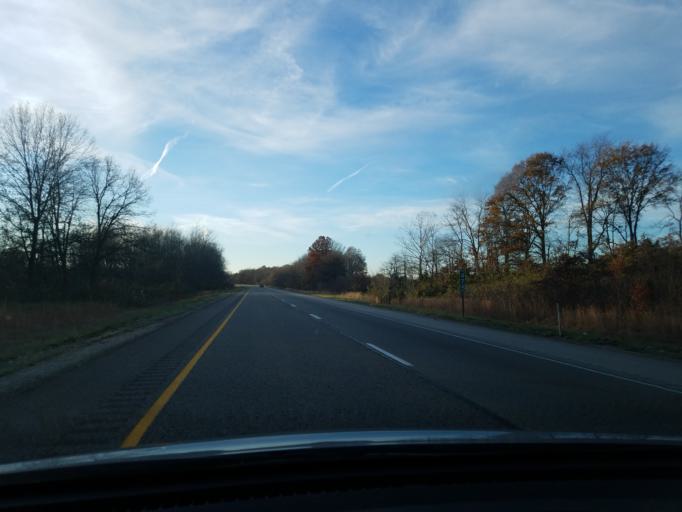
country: US
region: Indiana
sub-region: Spencer County
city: Dale
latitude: 38.1976
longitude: -87.1459
